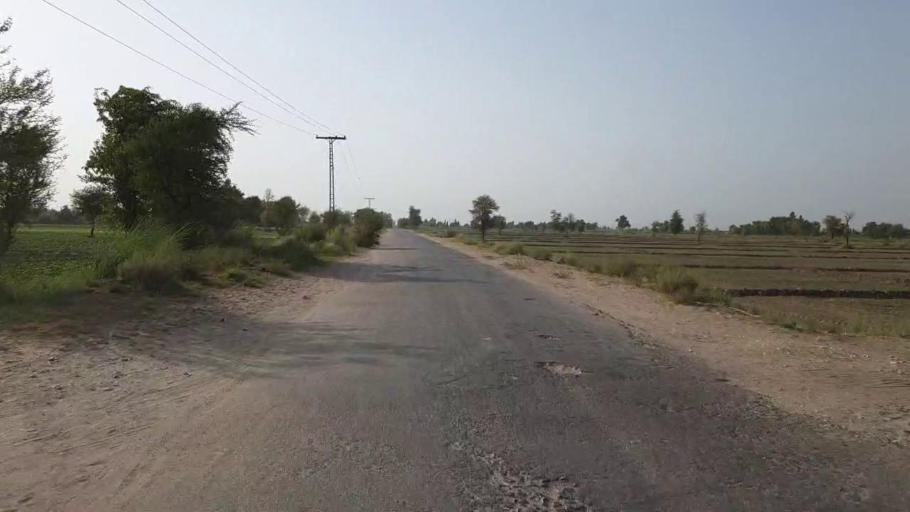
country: PK
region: Sindh
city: Jam Sahib
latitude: 26.3844
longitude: 68.8841
